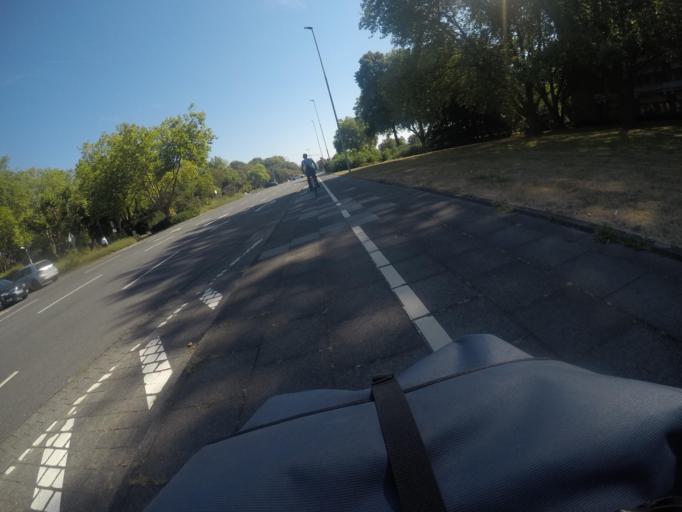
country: DE
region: North Rhine-Westphalia
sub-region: Regierungsbezirk Koln
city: Leverkusen
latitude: 51.0109
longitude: 6.9918
